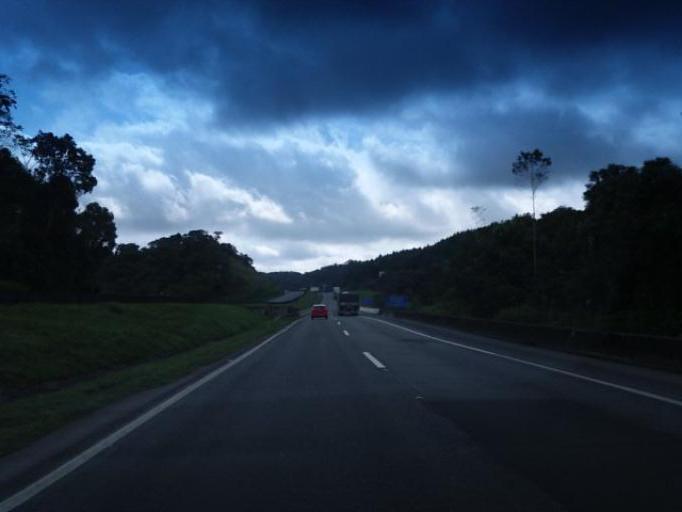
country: BR
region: Parana
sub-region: Antonina
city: Antonina
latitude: -25.0997
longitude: -48.6907
